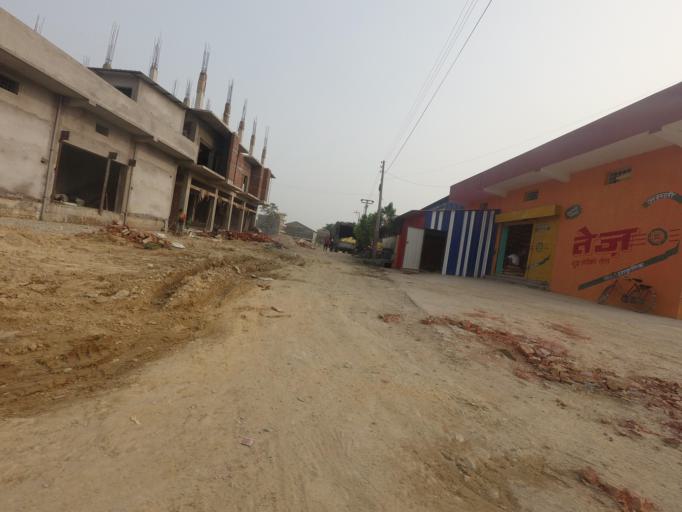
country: NP
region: Western Region
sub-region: Lumbini Zone
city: Bhairahawa
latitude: 27.5123
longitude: 83.4383
